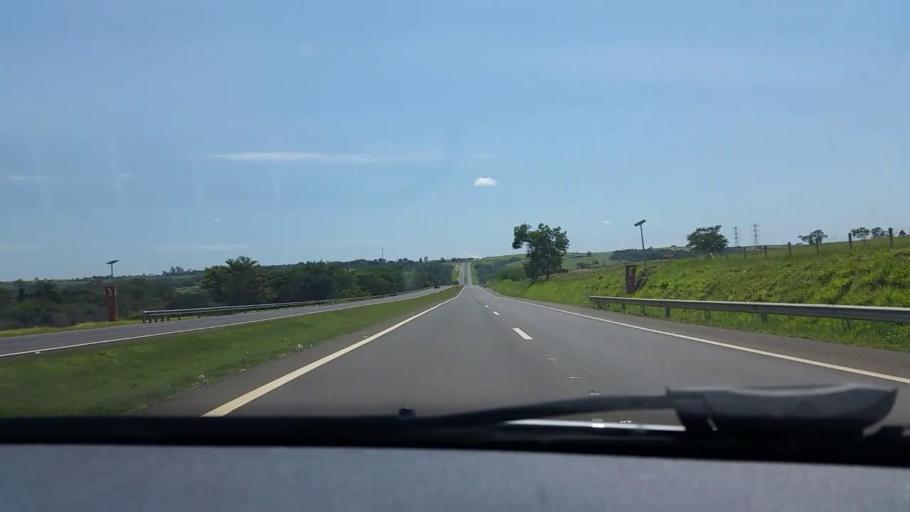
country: BR
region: Sao Paulo
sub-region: Bauru
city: Bauru
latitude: -22.4140
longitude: -49.1058
